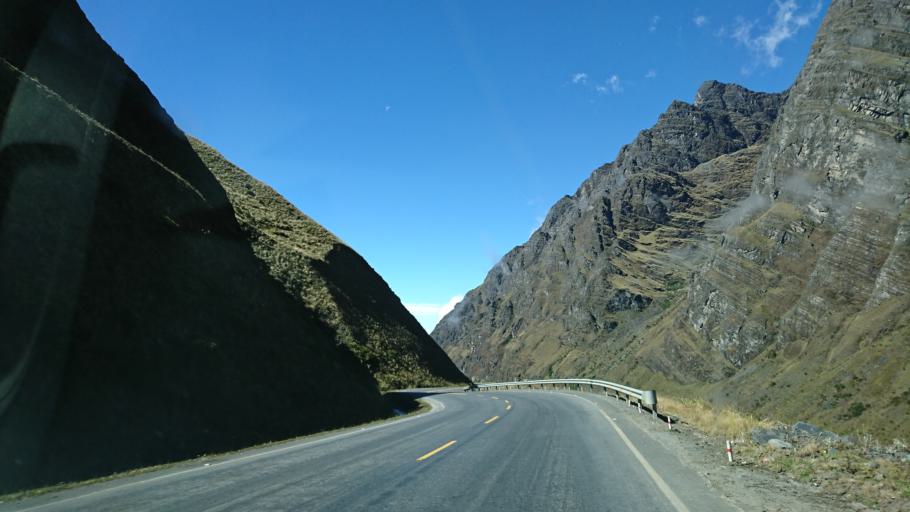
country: BO
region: La Paz
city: Coroico
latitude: -16.3283
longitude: -67.9468
